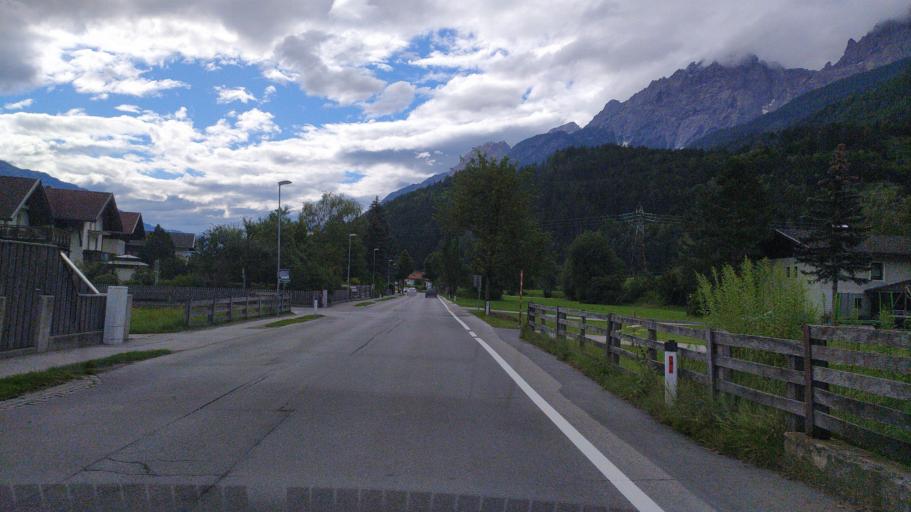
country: AT
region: Tyrol
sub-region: Politischer Bezirk Lienz
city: Tristach
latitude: 46.8182
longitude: 12.7942
